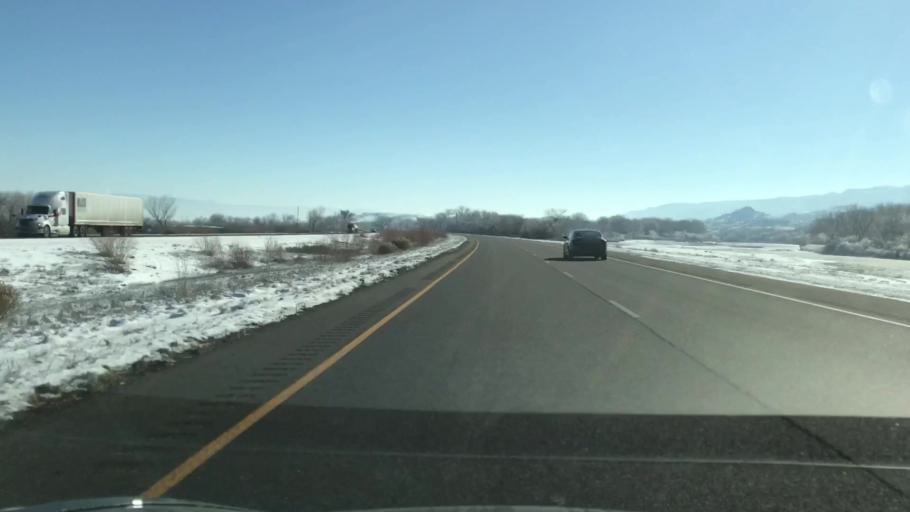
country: US
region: Colorado
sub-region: Mesa County
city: Loma
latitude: 39.1688
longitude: -108.7919
